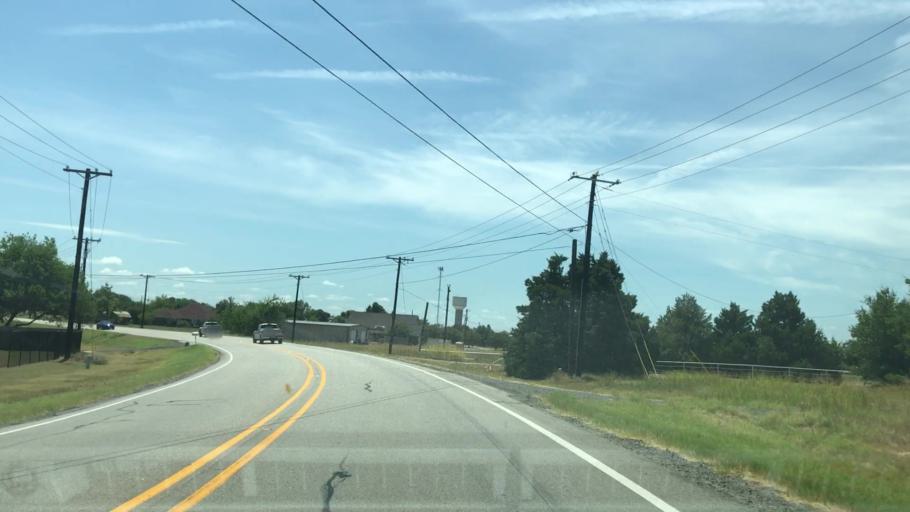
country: US
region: Texas
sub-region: Collin County
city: Saint Paul
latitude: 33.0358
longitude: -96.5503
